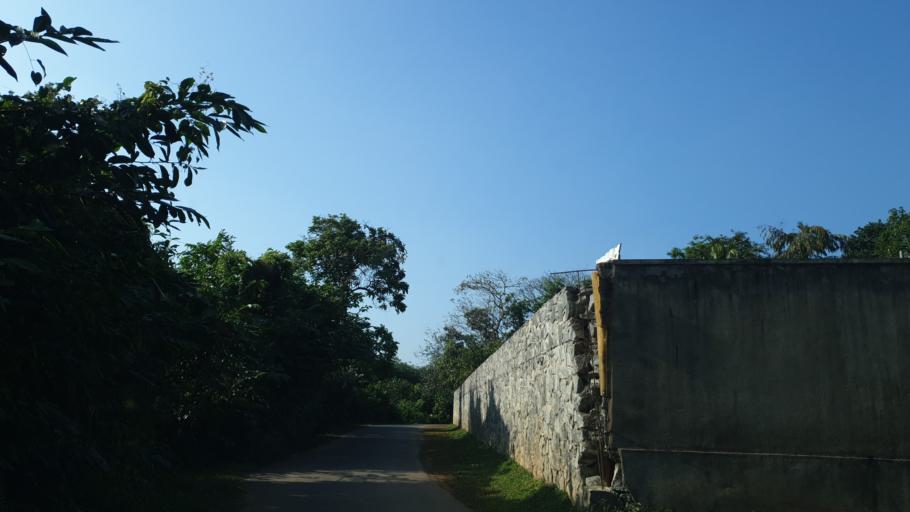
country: LK
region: Western
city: Battaramulla South
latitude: 6.8853
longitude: 79.9484
